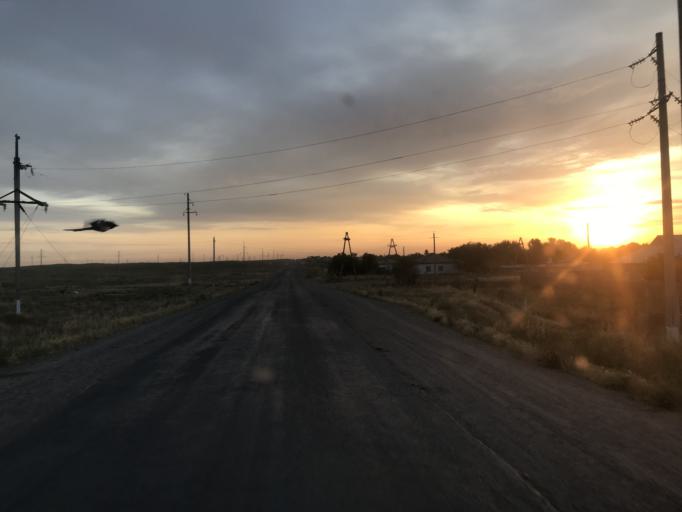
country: UZ
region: Toshkent
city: Chinoz
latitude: 41.1342
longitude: 68.7216
